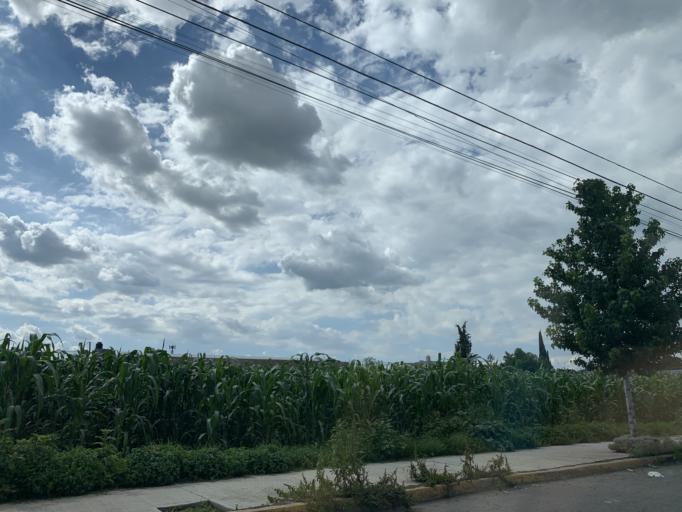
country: MX
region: Puebla
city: Cholula
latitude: 19.0603
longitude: -98.3197
